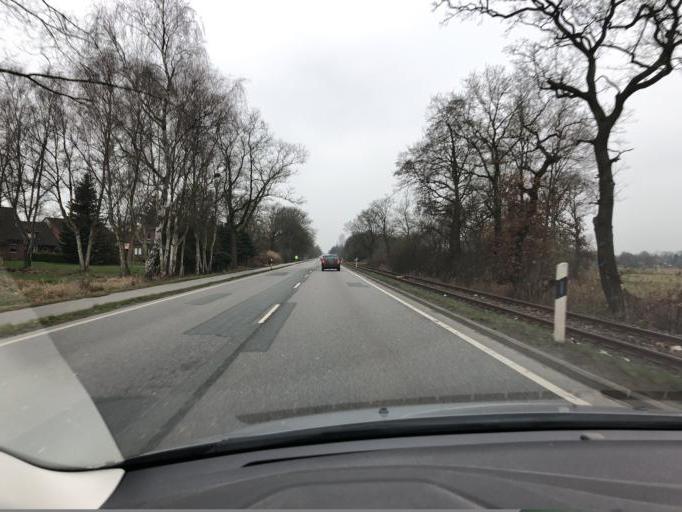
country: DE
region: Lower Saxony
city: Aurich
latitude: 53.4721
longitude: 7.4531
